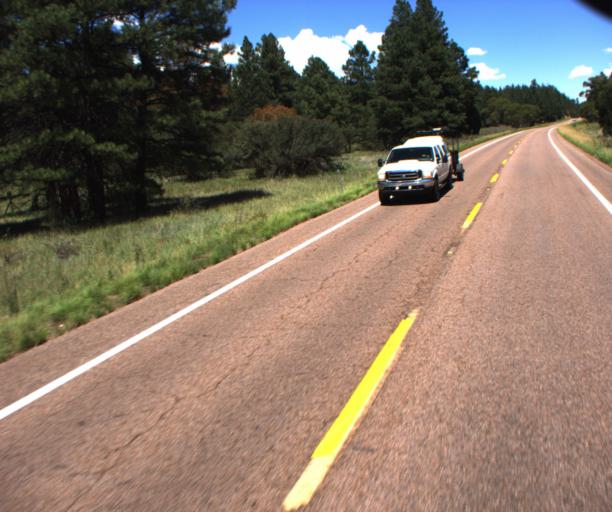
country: US
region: Arizona
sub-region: Navajo County
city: Lake of the Woods
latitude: 34.1410
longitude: -110.1057
